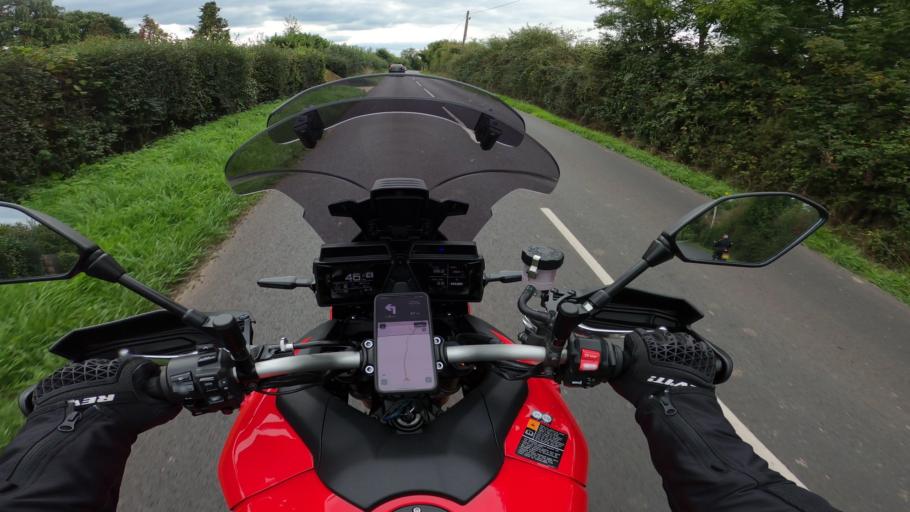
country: GB
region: England
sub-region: Kent
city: Edenbridge
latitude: 51.1936
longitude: 0.0358
